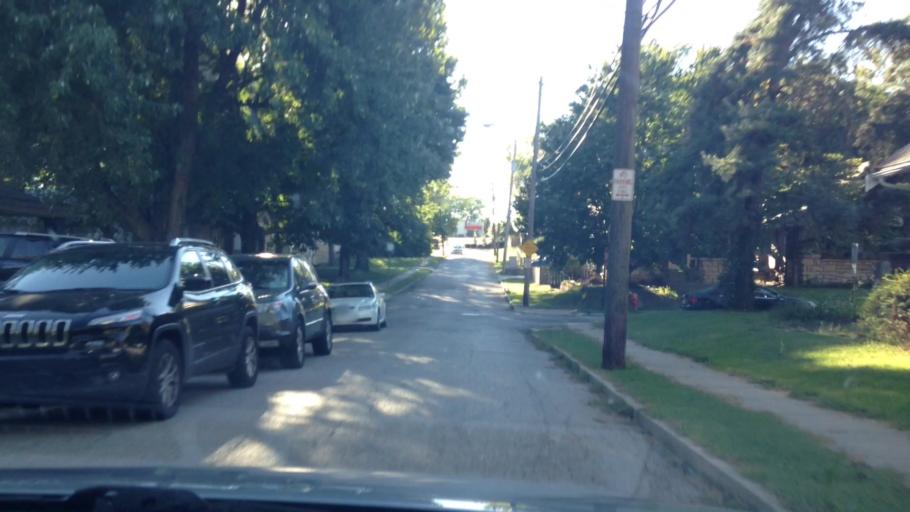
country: US
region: Kansas
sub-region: Johnson County
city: Westwood
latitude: 39.0511
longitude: -94.6091
